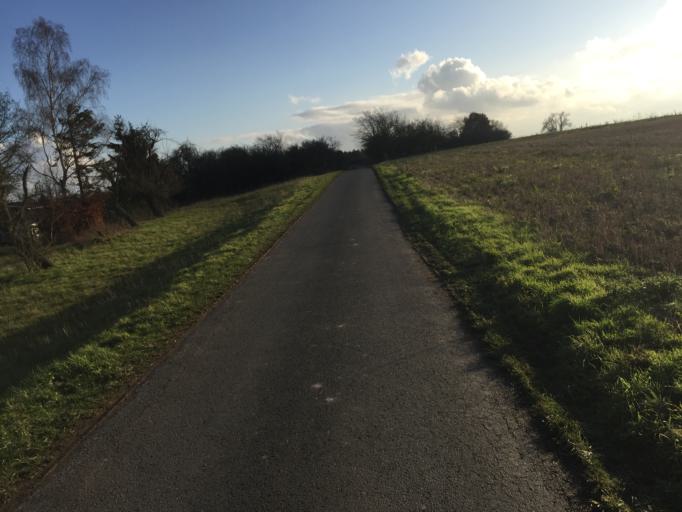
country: DE
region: Hesse
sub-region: Regierungsbezirk Giessen
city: Langgons
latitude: 50.5206
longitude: 8.7115
